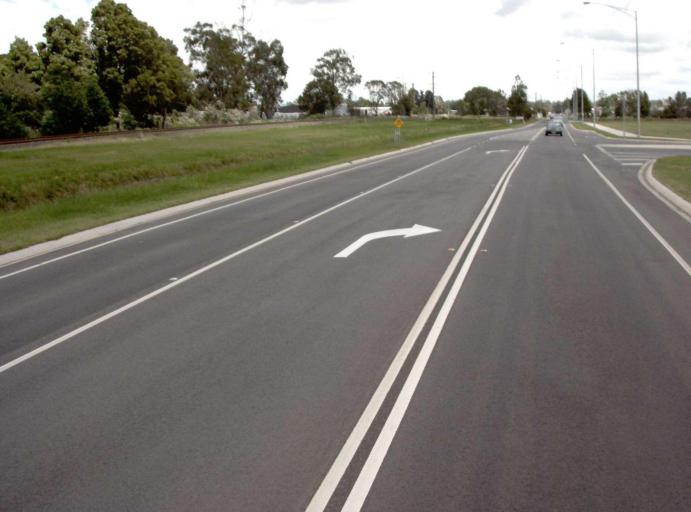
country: AU
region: Victoria
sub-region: Baw Baw
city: Warragul
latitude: -38.1677
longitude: 145.9532
